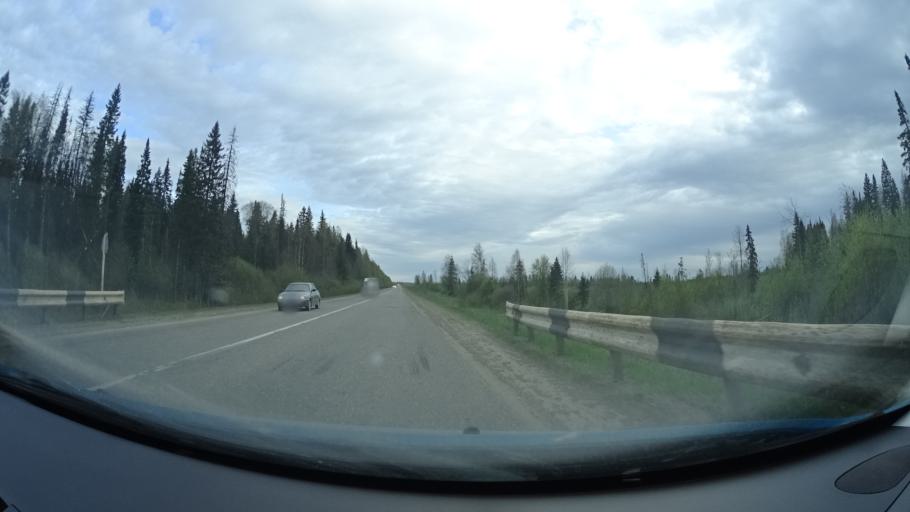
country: RU
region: Perm
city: Osa
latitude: 57.3886
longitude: 55.6082
